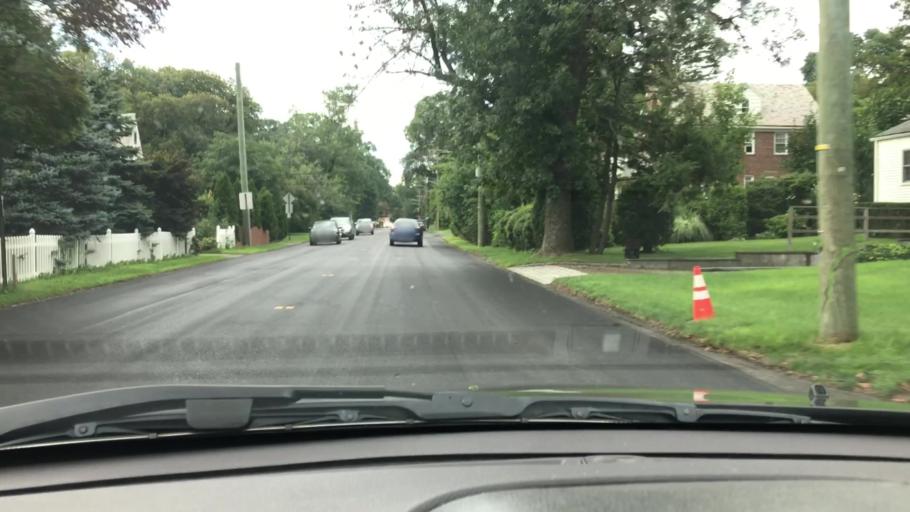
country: US
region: New York
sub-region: Westchester County
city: Pelham
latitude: 40.9381
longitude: -73.7983
